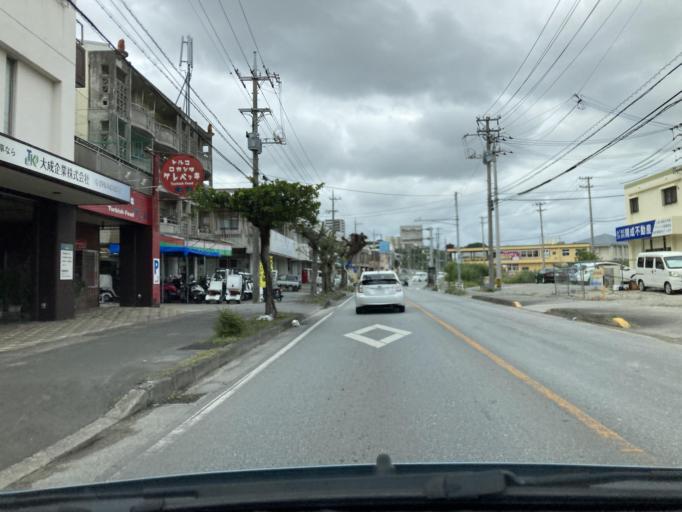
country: JP
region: Okinawa
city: Ginowan
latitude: 26.2390
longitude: 127.7462
